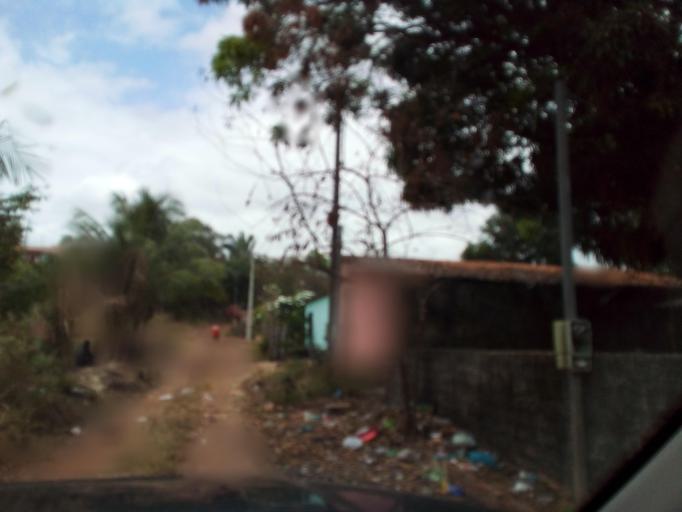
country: BR
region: Maranhao
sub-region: Sao Luis
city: Sao Luis
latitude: -2.6722
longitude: -44.2933
